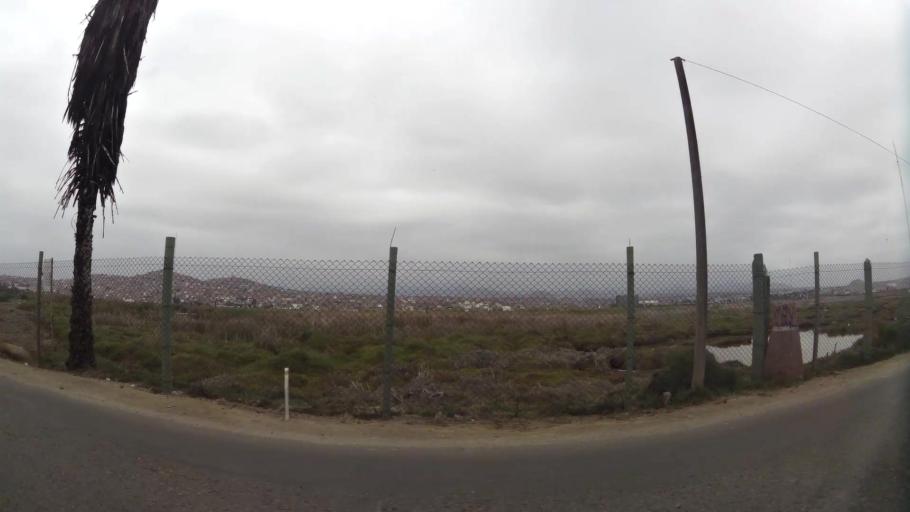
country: PE
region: Lima
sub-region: Lima
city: Surco
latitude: -12.2094
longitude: -76.9973
